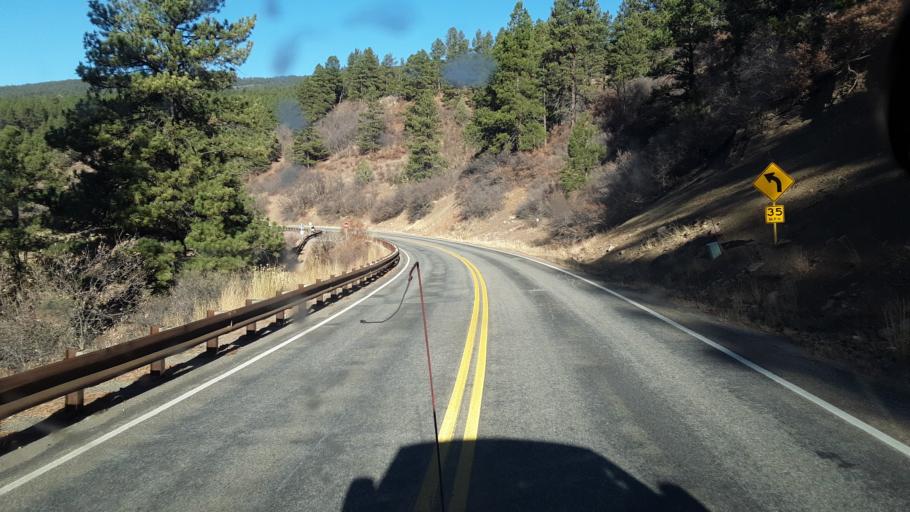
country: US
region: Colorado
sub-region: La Plata County
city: Durango
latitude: 37.3322
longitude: -107.7380
